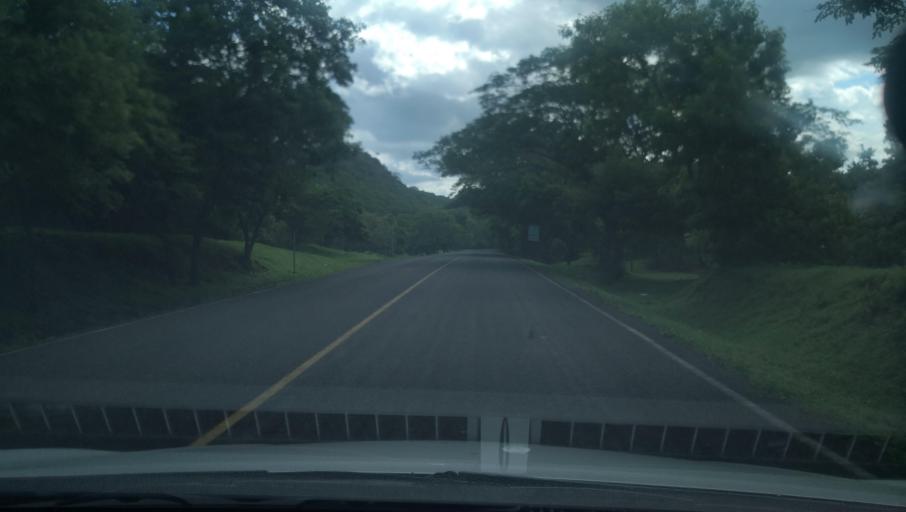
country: NI
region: Madriz
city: Somoto
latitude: 13.4648
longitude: -86.6402
